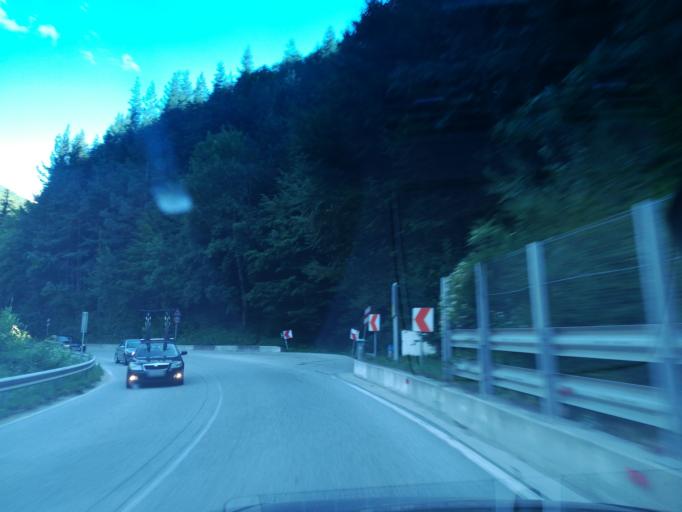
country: BG
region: Smolyan
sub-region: Obshtina Chepelare
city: Chepelare
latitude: 41.7980
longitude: 24.7087
